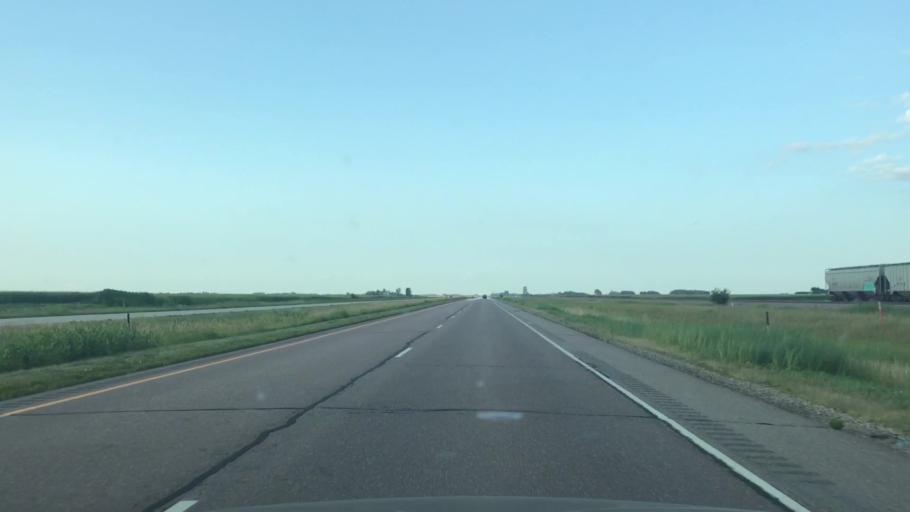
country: US
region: Minnesota
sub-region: Nobles County
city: Worthington
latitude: 43.7266
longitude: -95.4284
